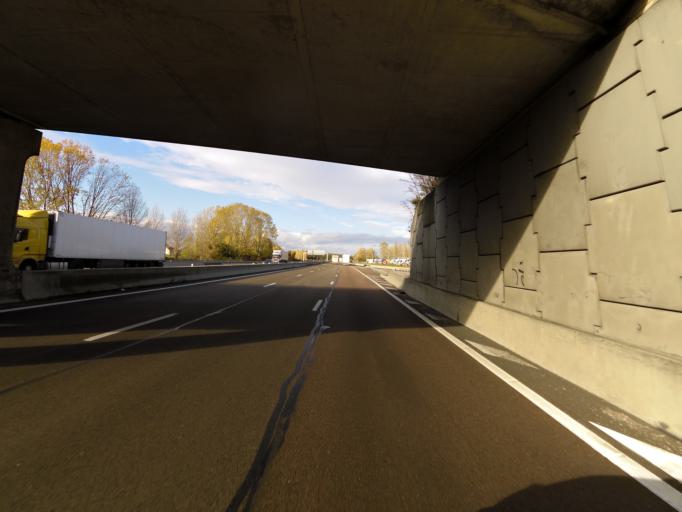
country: FR
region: Bourgogne
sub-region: Departement de la Cote-d'Or
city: Couternon
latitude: 47.3474
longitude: 5.1637
